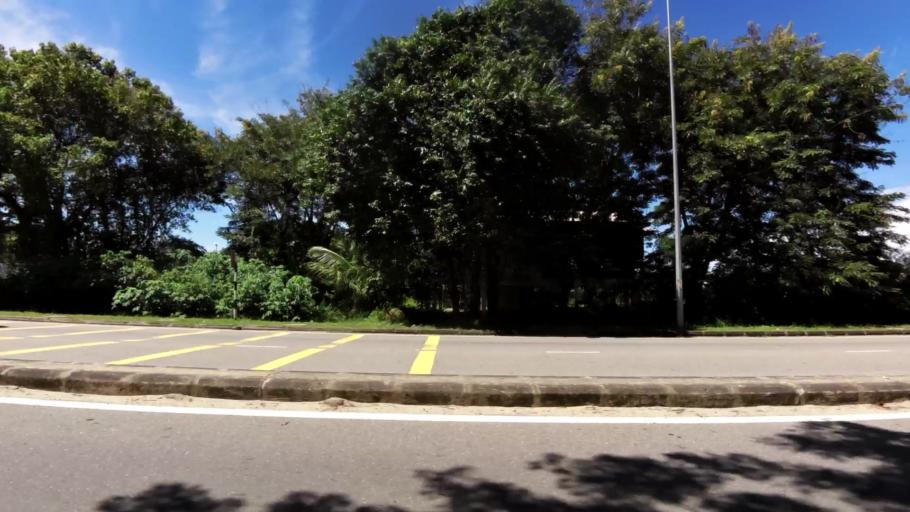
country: BN
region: Brunei and Muara
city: Bandar Seri Begawan
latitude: 5.0276
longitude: 115.0672
